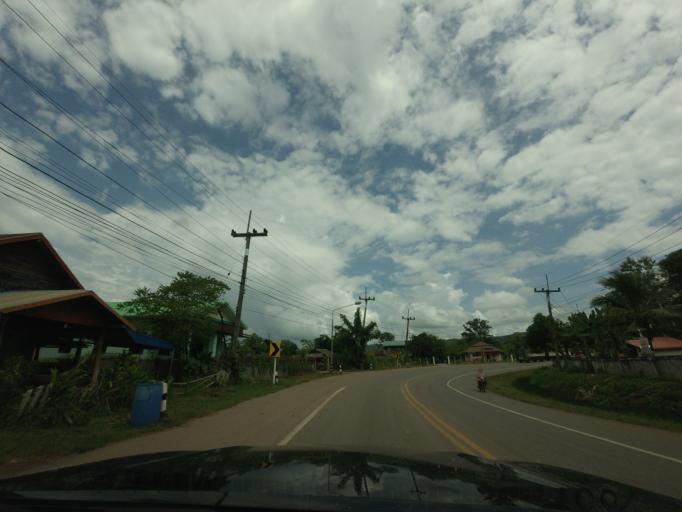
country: TH
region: Changwat Udon Thani
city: Nam Som
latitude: 17.8029
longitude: 102.2833
